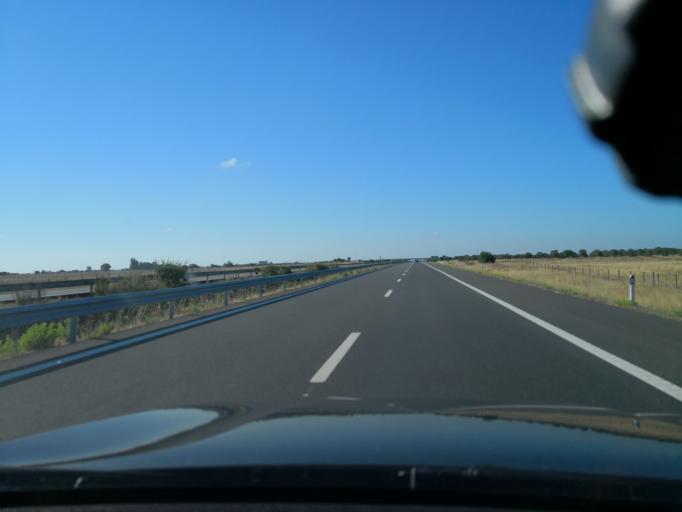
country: PT
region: Beja
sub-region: Aljustrel
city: Aljustrel
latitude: 38.0061
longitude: -8.2757
